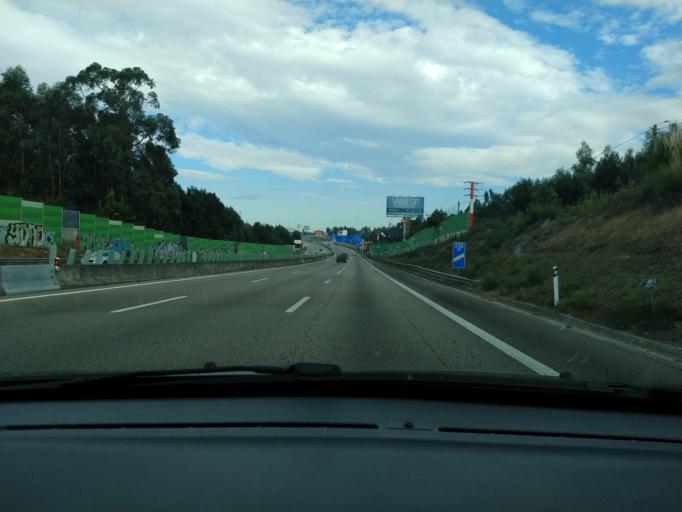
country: PT
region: Aveiro
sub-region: Santa Maria da Feira
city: Nogueira da Regedoura
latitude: 41.0014
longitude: -8.5830
